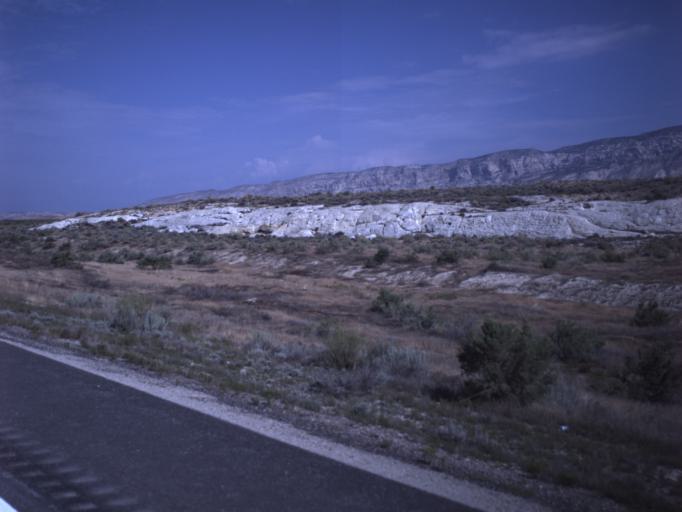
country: US
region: Colorado
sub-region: Rio Blanco County
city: Rangely
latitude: 40.2866
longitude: -109.1358
